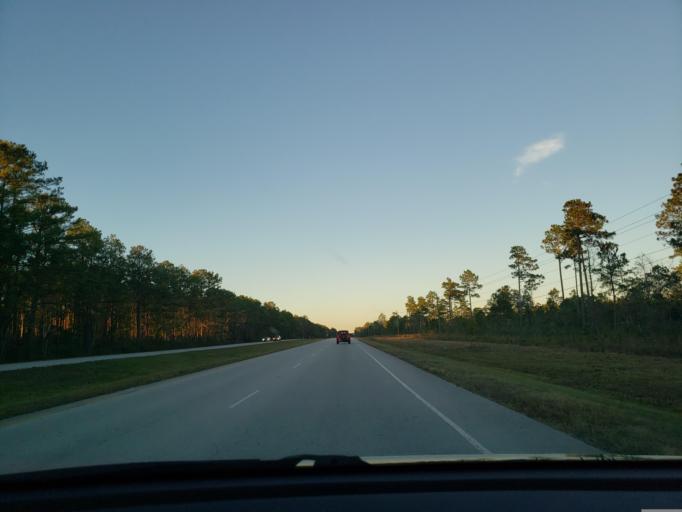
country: US
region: North Carolina
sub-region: Onslow County
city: Sneads Ferry
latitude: 34.6413
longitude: -77.4785
